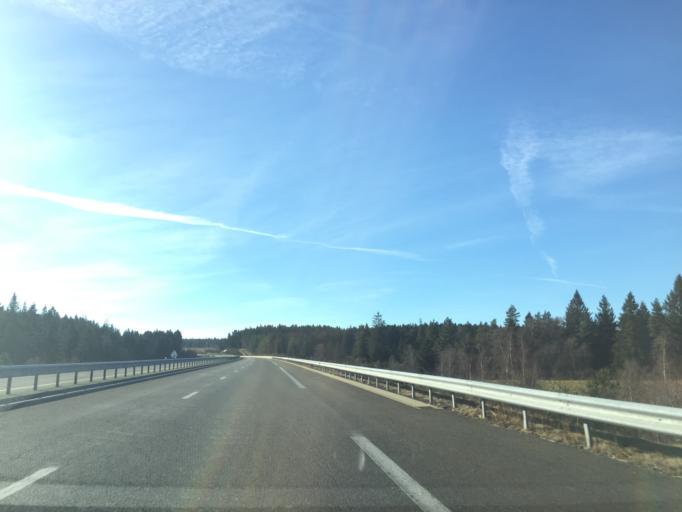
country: FR
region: Auvergne
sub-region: Departement du Puy-de-Dome
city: Gelles
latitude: 45.7521
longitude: 2.7206
